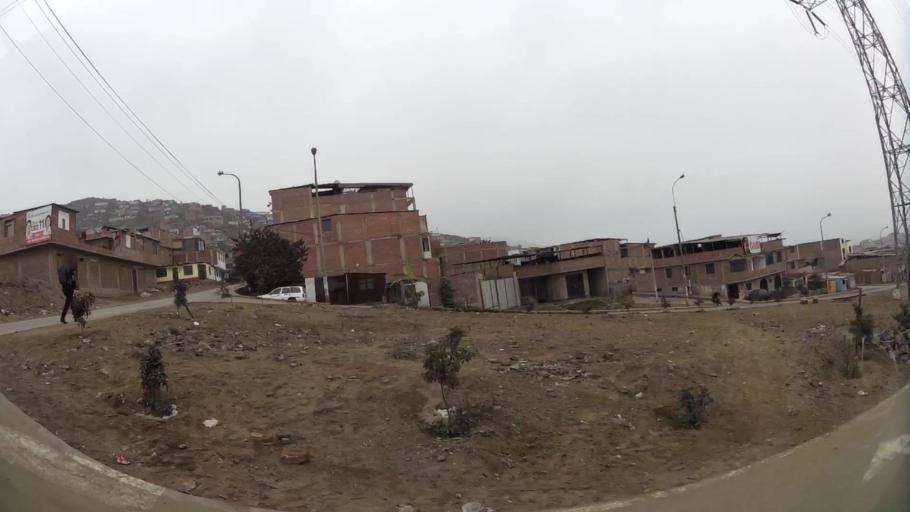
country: PE
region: Lima
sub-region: Lima
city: Surco
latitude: -12.2177
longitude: -76.9183
